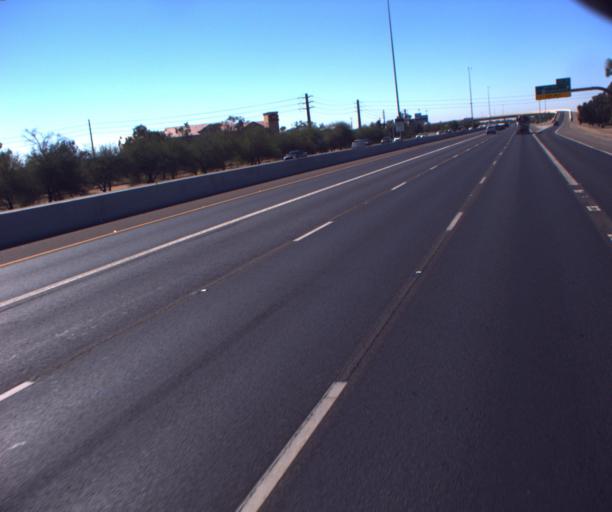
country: US
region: Arizona
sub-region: Maricopa County
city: Sun City
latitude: 33.6047
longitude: -112.2510
